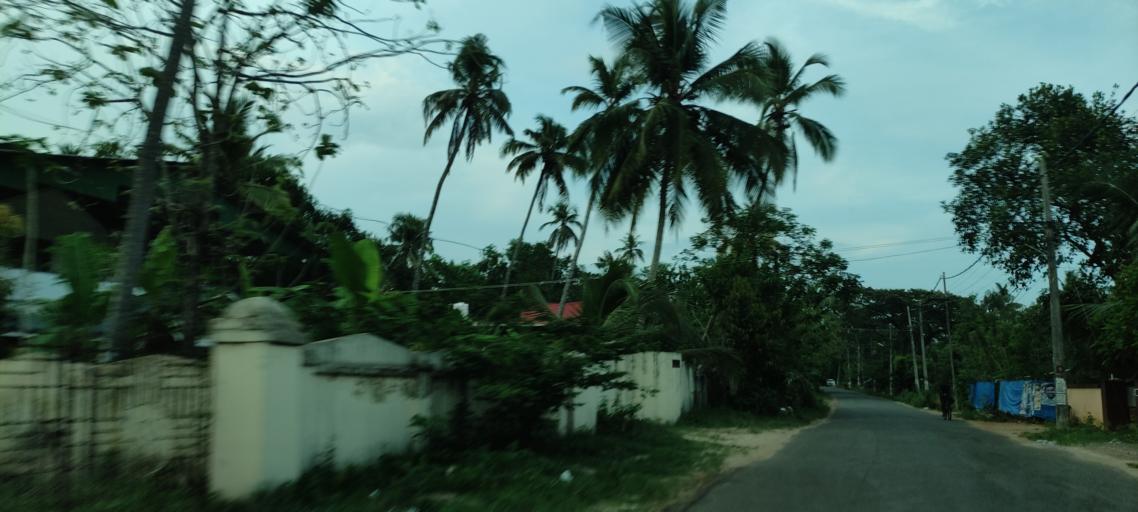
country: IN
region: Kerala
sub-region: Alappuzha
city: Shertallai
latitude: 9.7022
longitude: 76.3562
